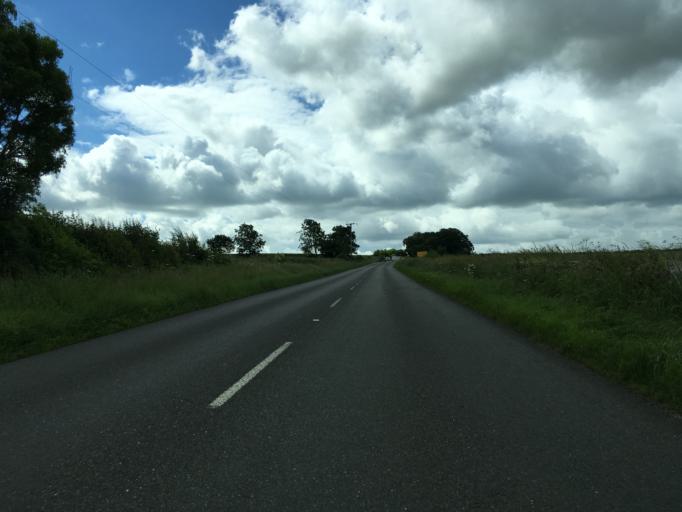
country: GB
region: England
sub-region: Oxfordshire
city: Shipton under Wychwood
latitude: 51.8457
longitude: -1.6024
